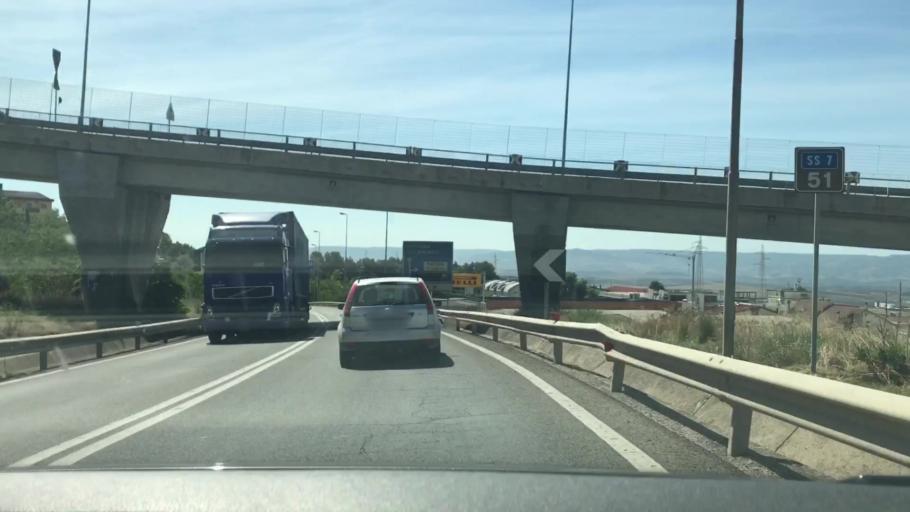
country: IT
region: Basilicate
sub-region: Provincia di Matera
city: Matera
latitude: 40.6732
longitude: 16.5775
